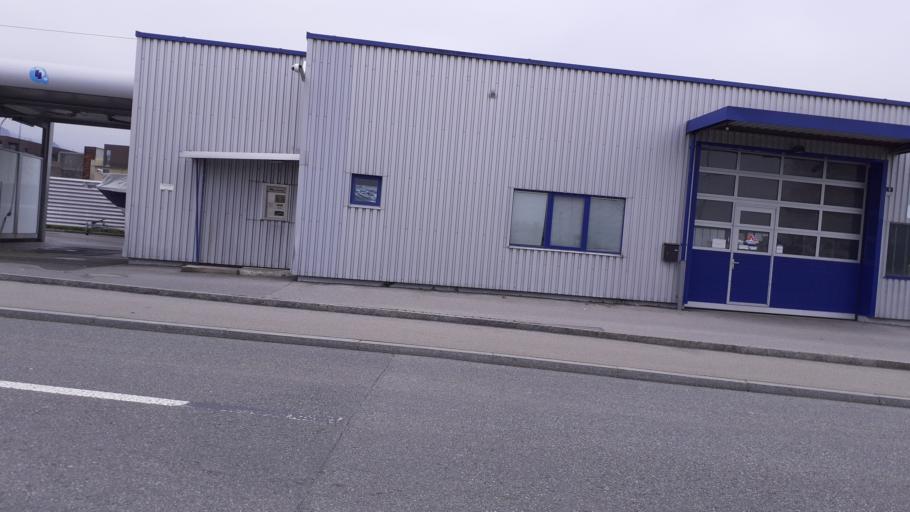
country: CH
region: Saint Gallen
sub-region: Wahlkreis Rheintal
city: Au
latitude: 47.4242
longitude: 9.6390
